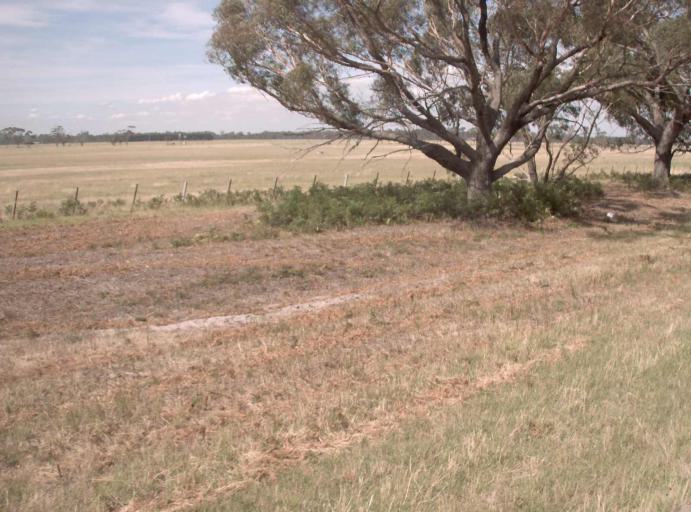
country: AU
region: Victoria
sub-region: Wellington
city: Sale
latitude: -38.1627
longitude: 146.8977
